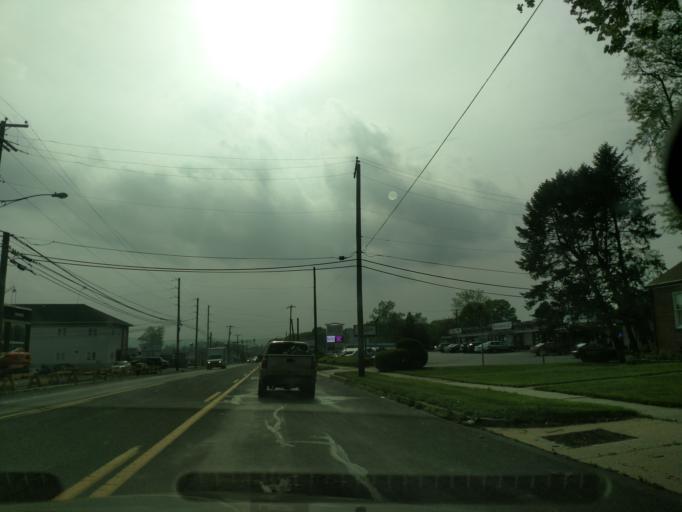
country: US
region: Pennsylvania
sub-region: Berks County
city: Sinking Spring
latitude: 40.3258
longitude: -76.0056
